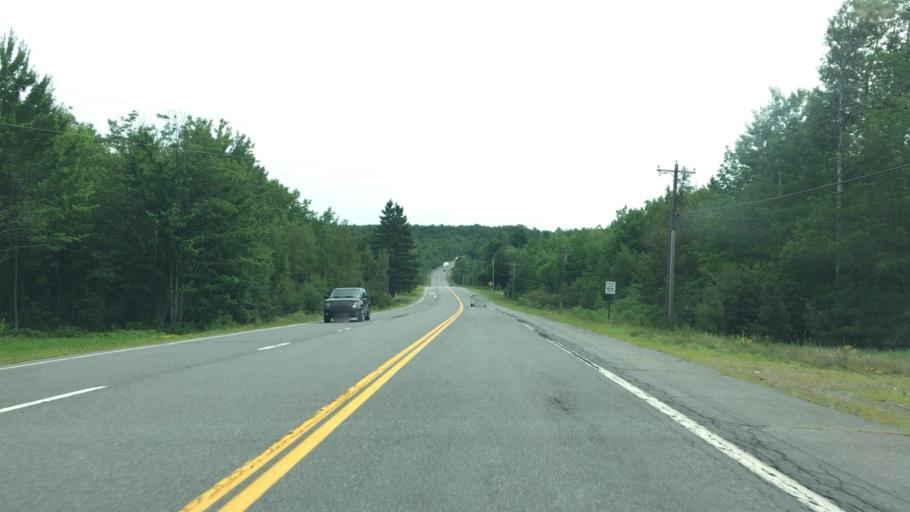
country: US
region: Maine
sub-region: Washington County
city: Calais
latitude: 45.0885
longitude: -67.4952
